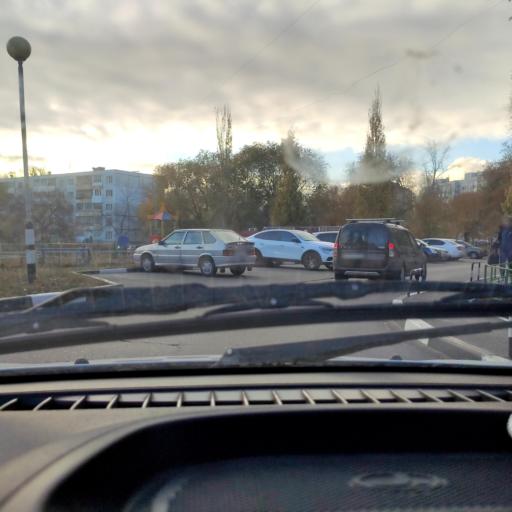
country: RU
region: Samara
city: Zhigulevsk
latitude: 53.4861
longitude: 49.4658
